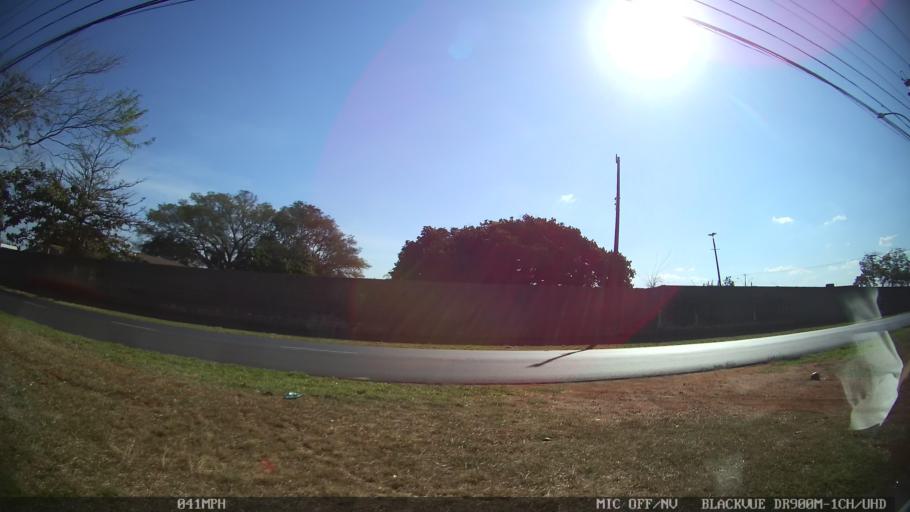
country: BR
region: Sao Paulo
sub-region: Ribeirao Preto
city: Ribeirao Preto
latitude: -21.1510
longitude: -47.7672
